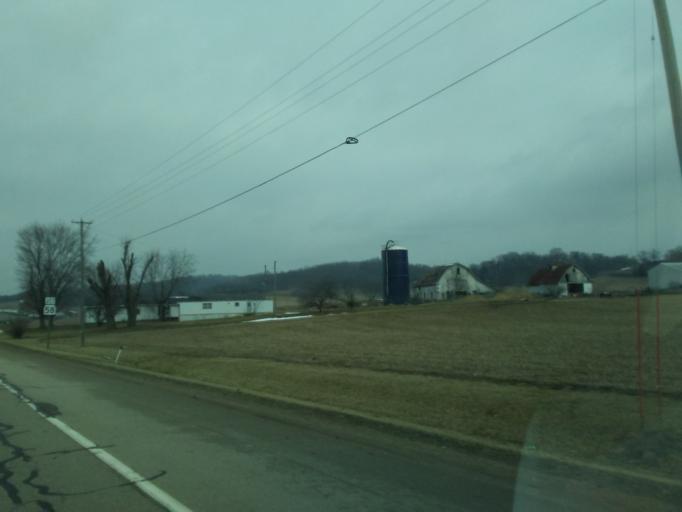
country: US
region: Wisconsin
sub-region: Richland County
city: Richland Center
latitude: 43.2958
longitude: -90.3249
